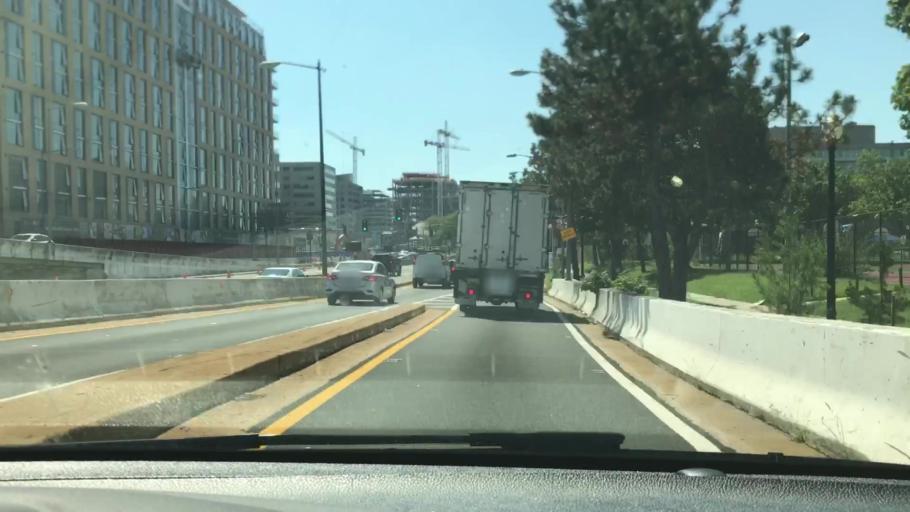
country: US
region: Washington, D.C.
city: Washington, D.C.
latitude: 38.8808
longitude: -77.0092
